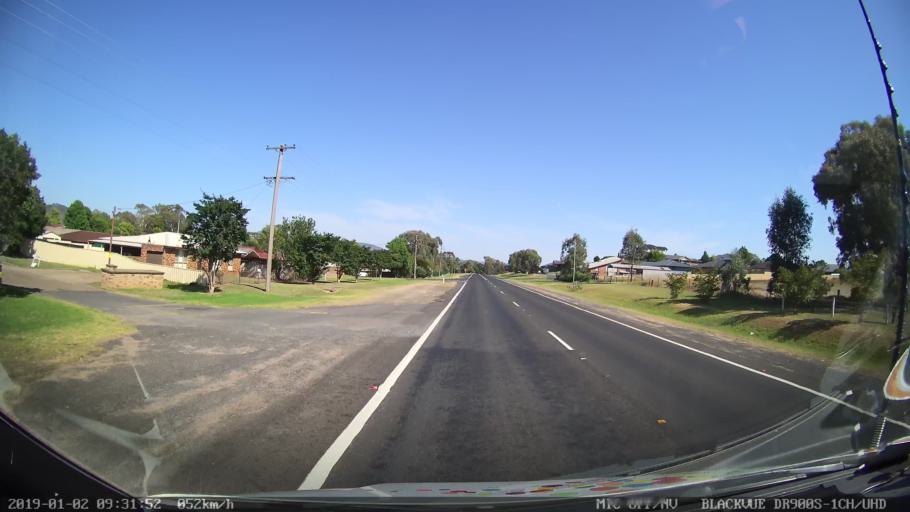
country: AU
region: New South Wales
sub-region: Tumut Shire
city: Tumut
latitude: -35.3158
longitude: 148.2330
